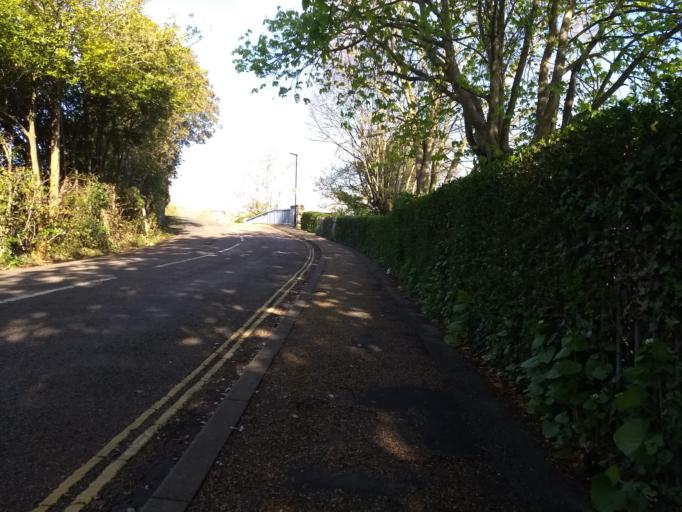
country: GB
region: England
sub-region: Isle of Wight
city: Ryde
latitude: 50.7272
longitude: -1.1523
